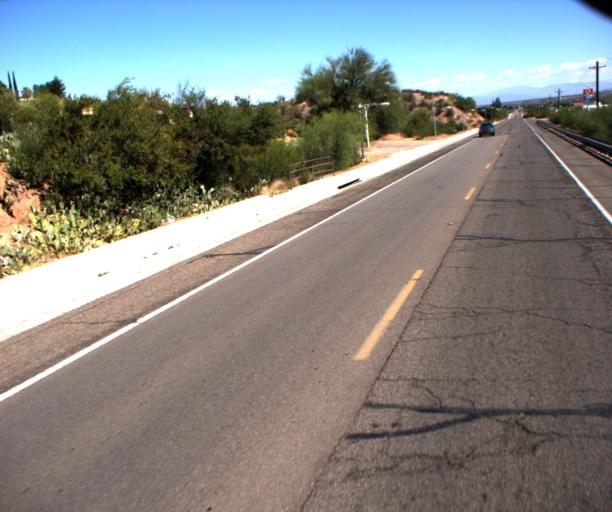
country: US
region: Arizona
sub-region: Pinal County
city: Mammoth
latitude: 32.7225
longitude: -110.6447
